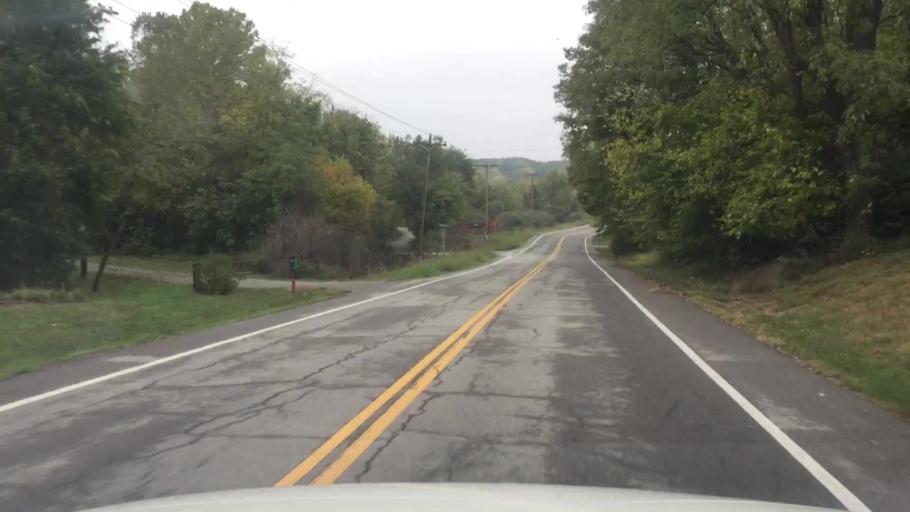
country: US
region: Missouri
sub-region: Boone County
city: Columbia
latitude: 38.8702
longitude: -92.4060
